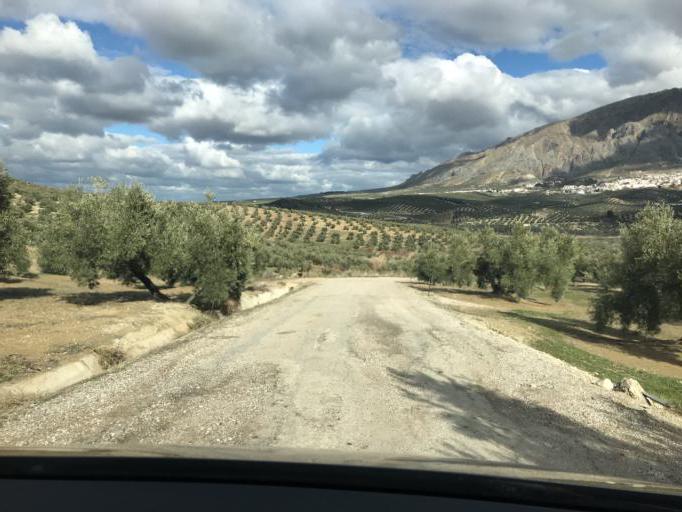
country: ES
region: Andalusia
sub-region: Provincia de Jaen
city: Jimena
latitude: 37.8144
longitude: -3.4407
